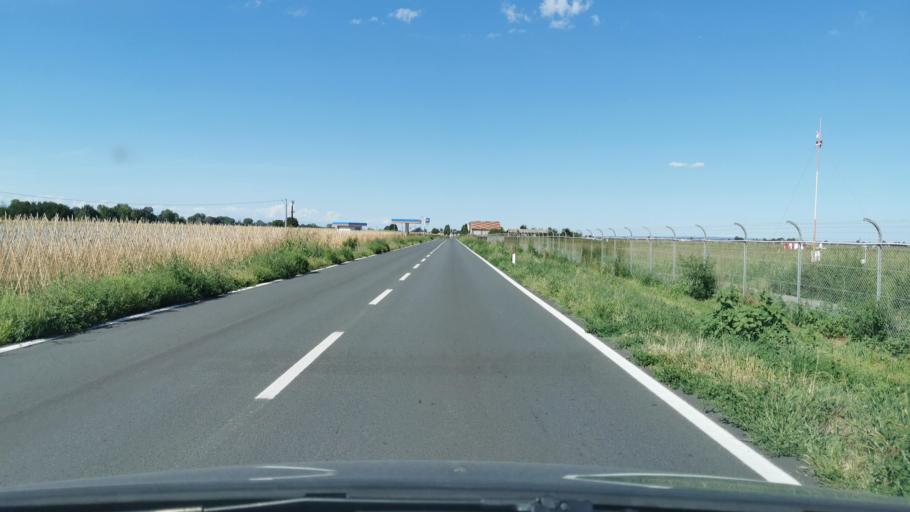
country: IT
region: Piedmont
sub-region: Provincia di Cuneo
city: Vottignasco
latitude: 44.5385
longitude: 7.6116
